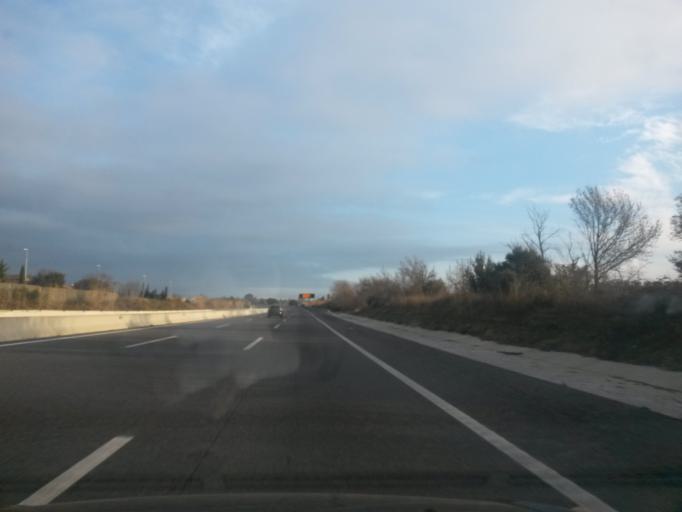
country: ES
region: Catalonia
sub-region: Provincia de Girona
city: Vilafant
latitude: 42.2460
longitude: 2.9405
